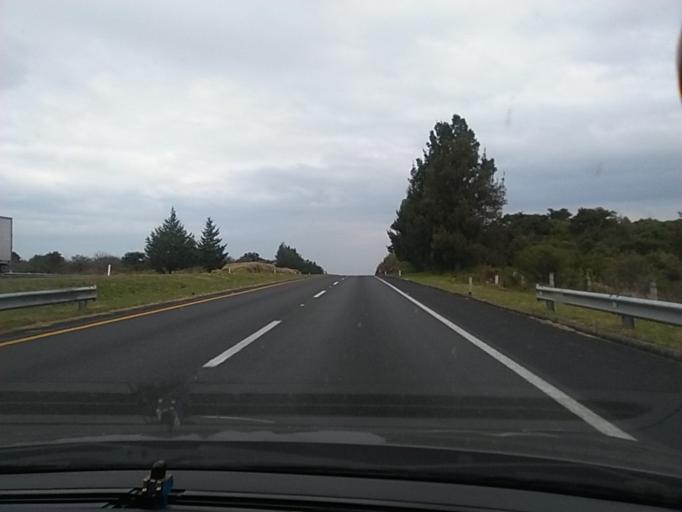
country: MX
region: Michoacan
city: Penjamillo de Degollado
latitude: 20.0822
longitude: -101.9892
